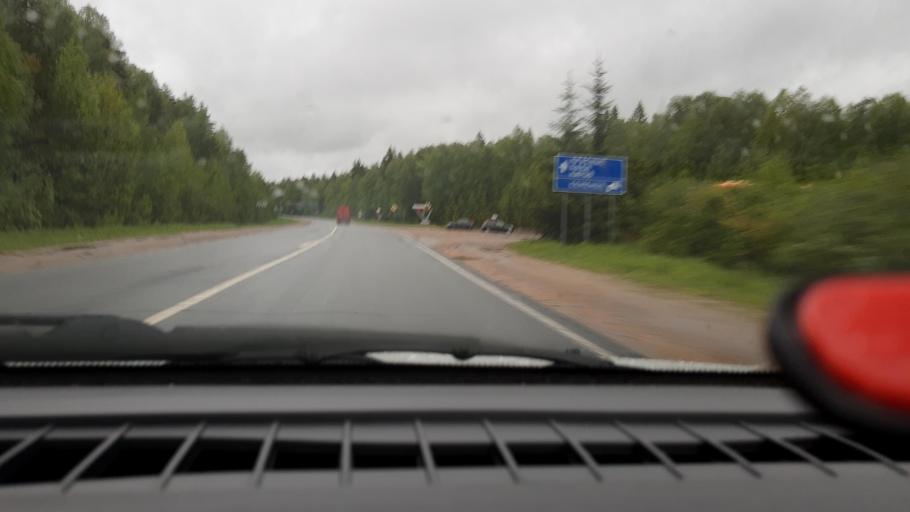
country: RU
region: Nizjnij Novgorod
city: Semenov
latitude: 56.8191
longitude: 44.5410
